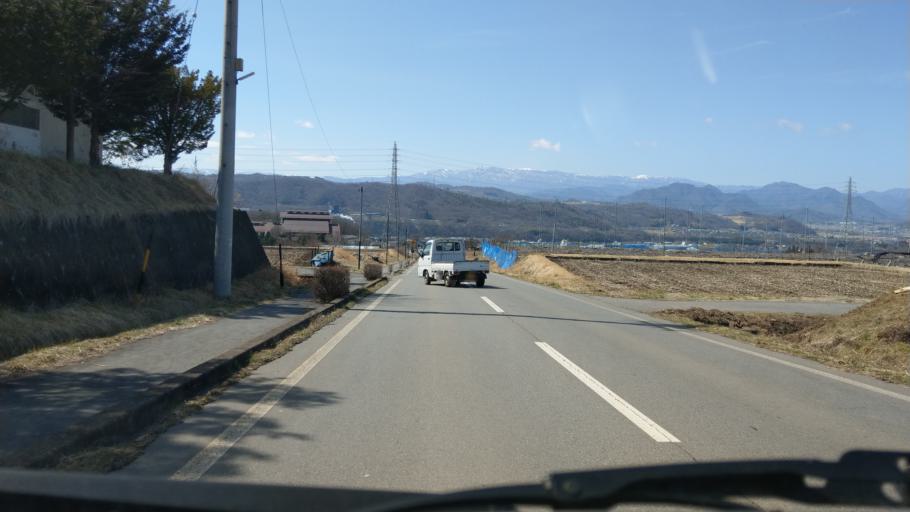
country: JP
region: Nagano
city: Ueda
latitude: 36.3644
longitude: 138.3432
